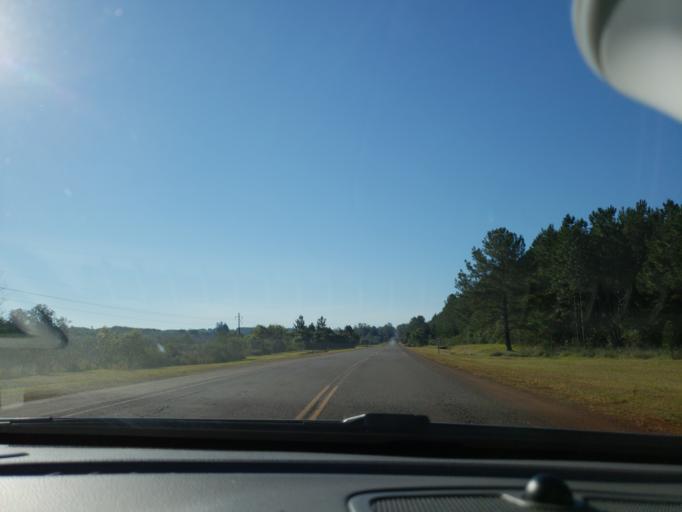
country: AR
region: Misiones
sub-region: Departamento de Apostoles
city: San Jose
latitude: -27.8264
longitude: -55.7708
